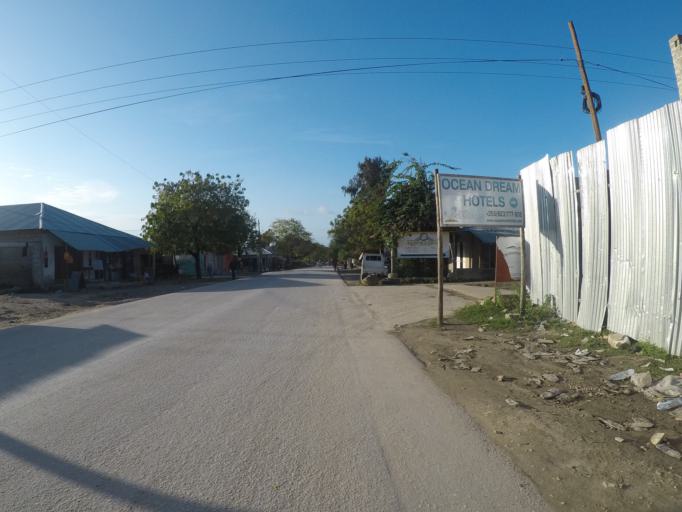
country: TZ
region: Zanzibar North
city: Nungwi
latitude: -5.7318
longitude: 39.2981
